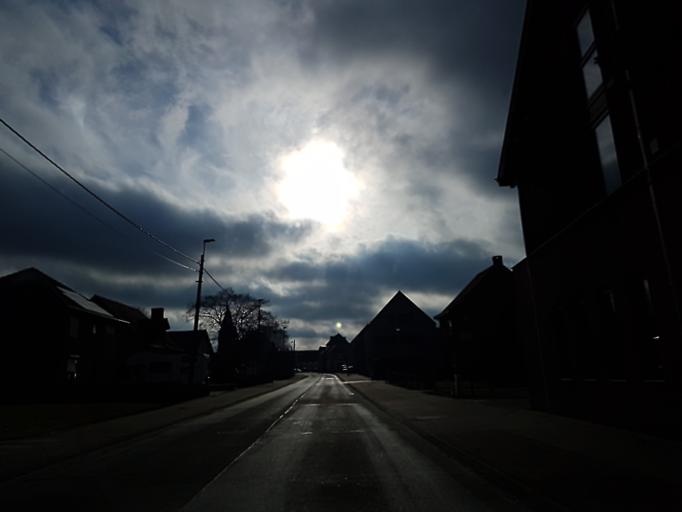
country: BE
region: Flanders
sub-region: Provincie Antwerpen
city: Hulshout
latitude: 51.0629
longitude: 4.8344
